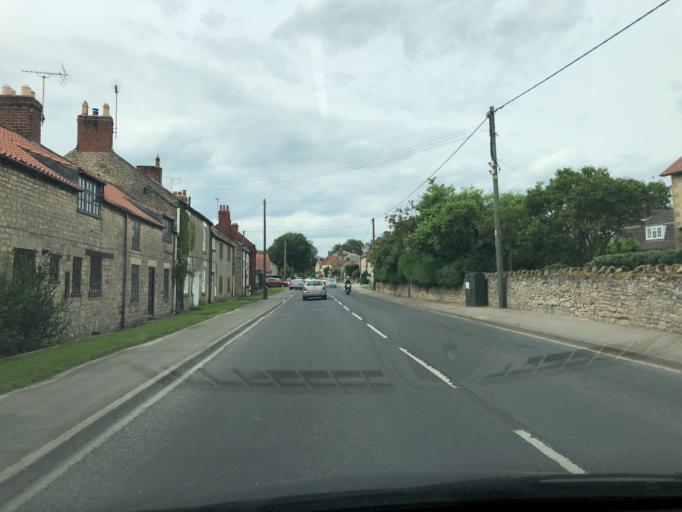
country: GB
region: England
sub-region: North Yorkshire
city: Pickering
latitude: 54.2562
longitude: -0.7977
